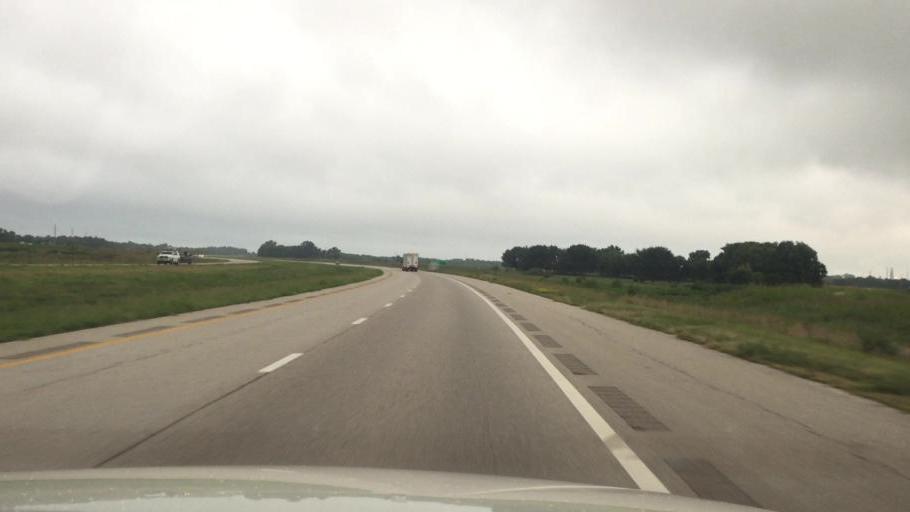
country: US
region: Kansas
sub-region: Montgomery County
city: Coffeyville
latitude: 37.0793
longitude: -95.5898
